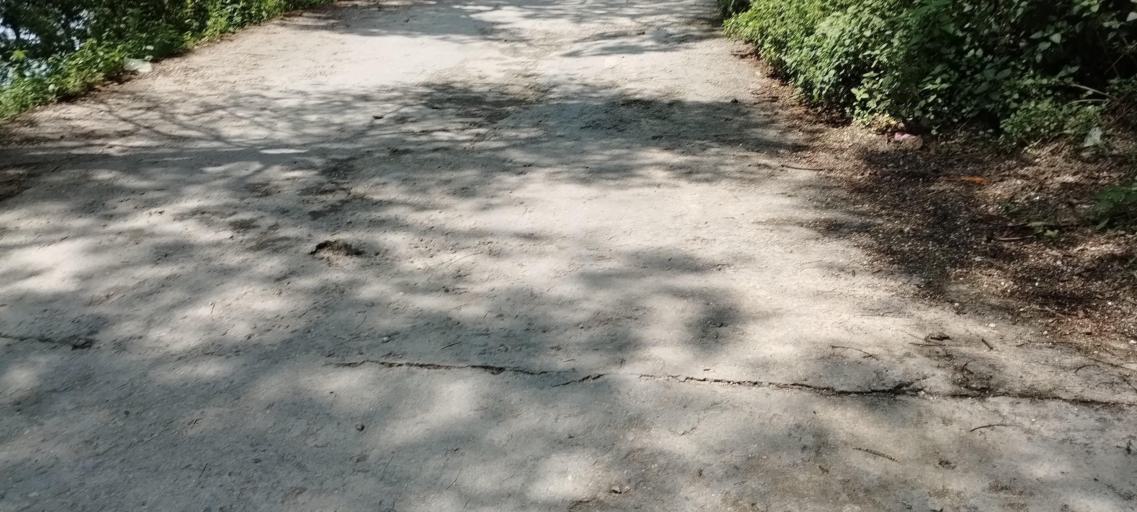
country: NP
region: Central Region
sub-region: Bagmati Zone
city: Kathmandu
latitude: 27.7885
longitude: 85.3620
